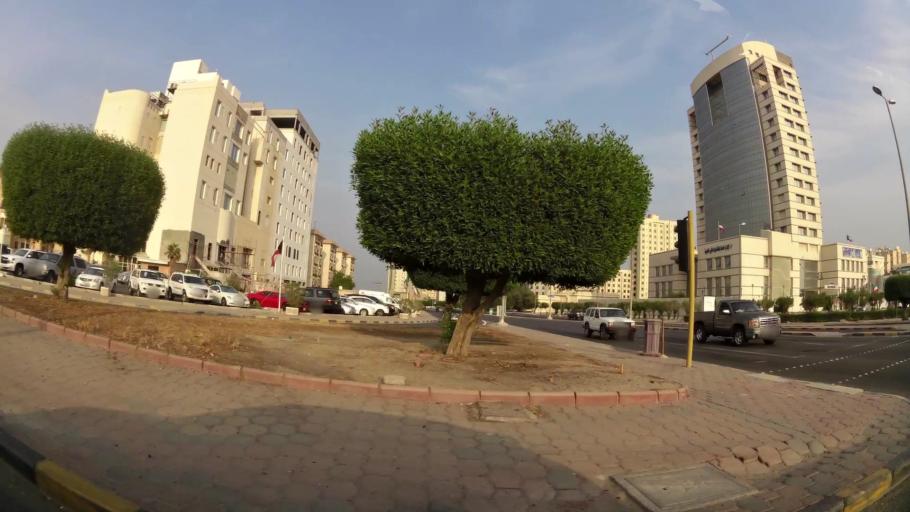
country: KW
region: Mubarak al Kabir
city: Sabah as Salim
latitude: 29.2502
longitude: 48.0807
